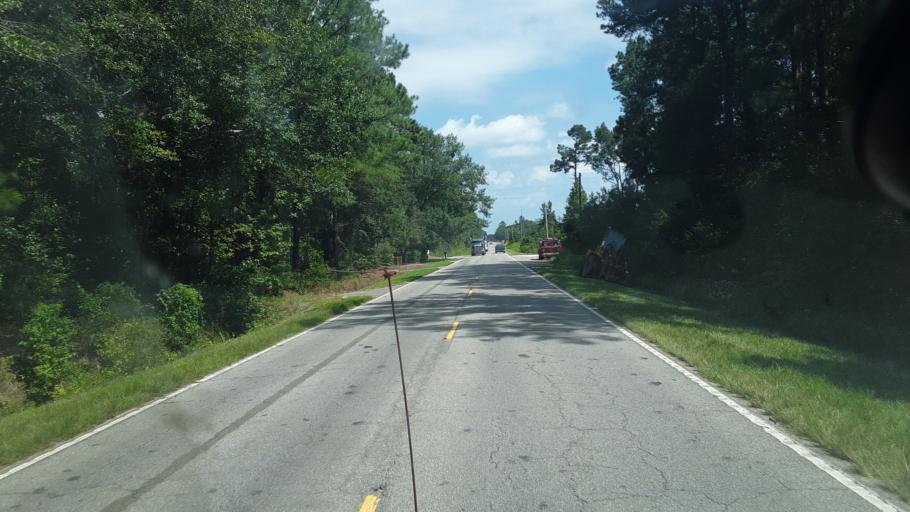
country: US
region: South Carolina
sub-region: Bamberg County
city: Bamberg
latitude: 33.2799
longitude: -81.0414
